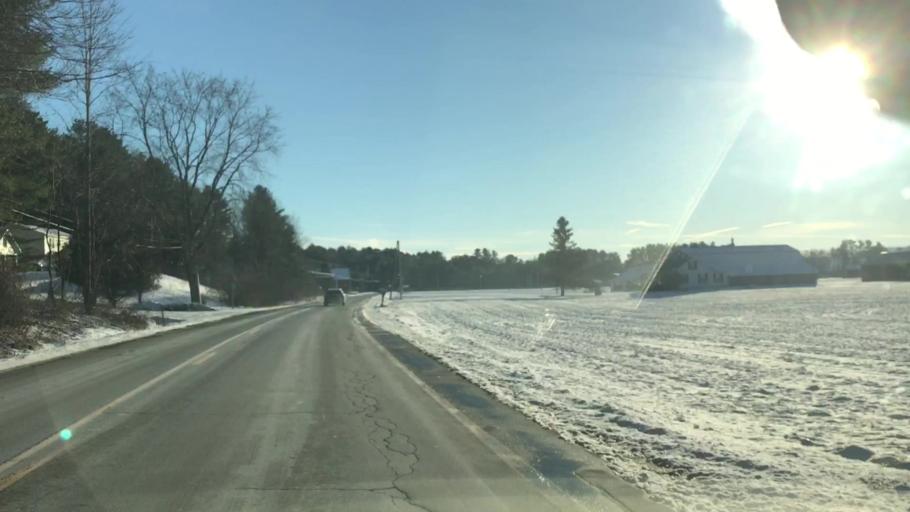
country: US
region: New Hampshire
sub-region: Grafton County
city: Haverhill
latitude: 44.0615
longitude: -72.0488
